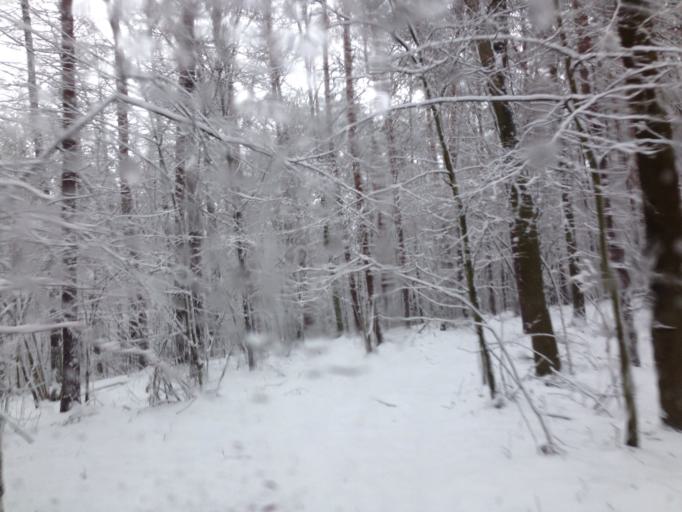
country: PL
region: Kujawsko-Pomorskie
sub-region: Powiat brodnicki
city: Gorzno
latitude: 53.1911
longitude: 19.6630
